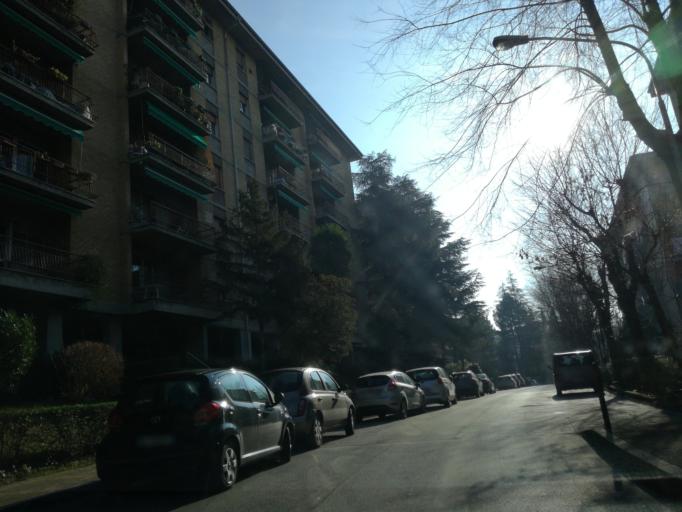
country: IT
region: Umbria
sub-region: Provincia di Perugia
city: Perugia
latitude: 43.1100
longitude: 12.3670
